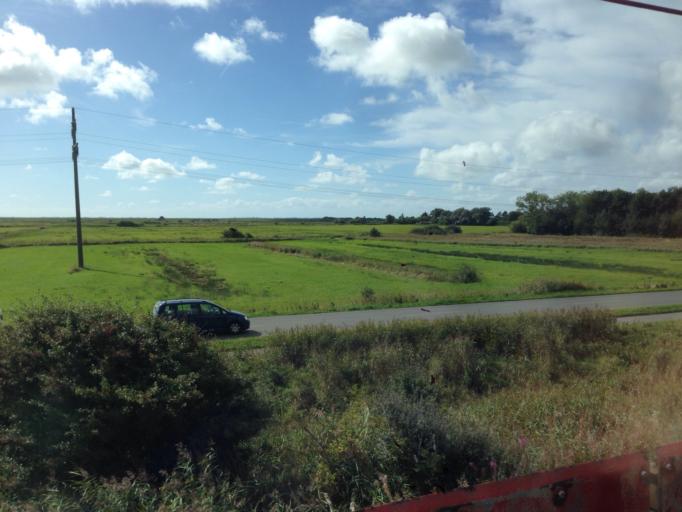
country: DE
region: Schleswig-Holstein
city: Keitum
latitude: 54.8855
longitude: 8.3778
